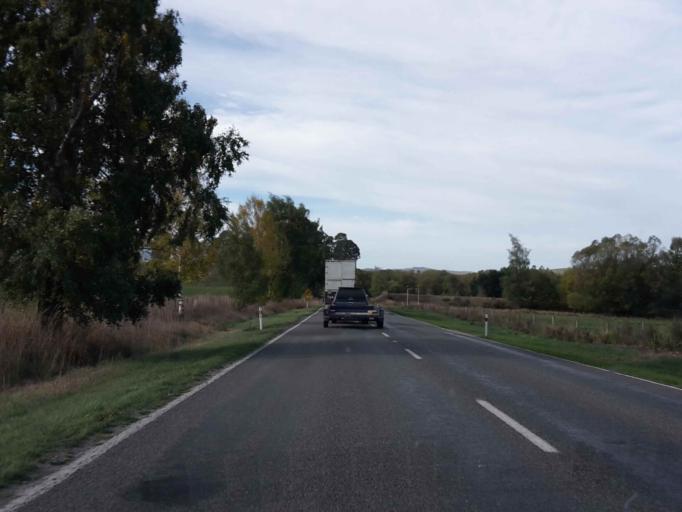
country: NZ
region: Canterbury
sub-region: Timaru District
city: Pleasant Point
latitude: -44.0930
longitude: 170.8432
